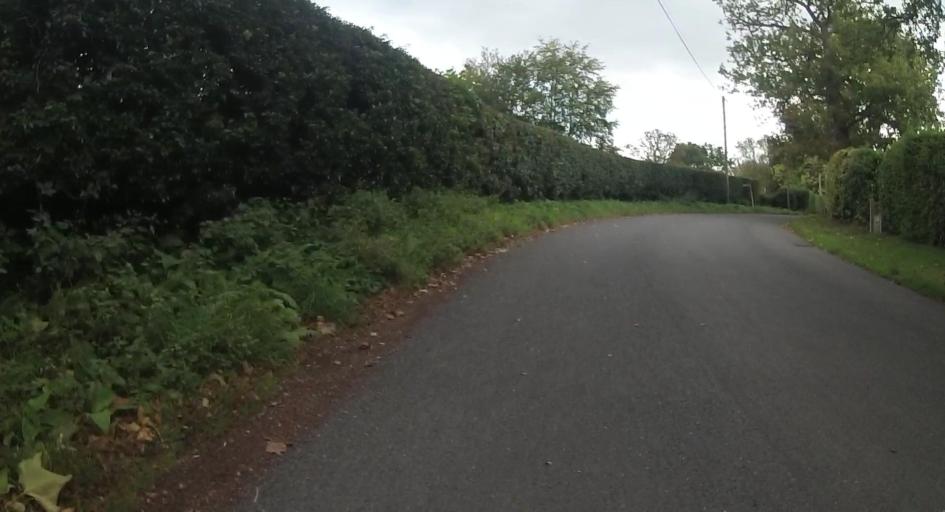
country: GB
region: England
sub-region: Hampshire
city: Hook
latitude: 51.3125
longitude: -0.9345
